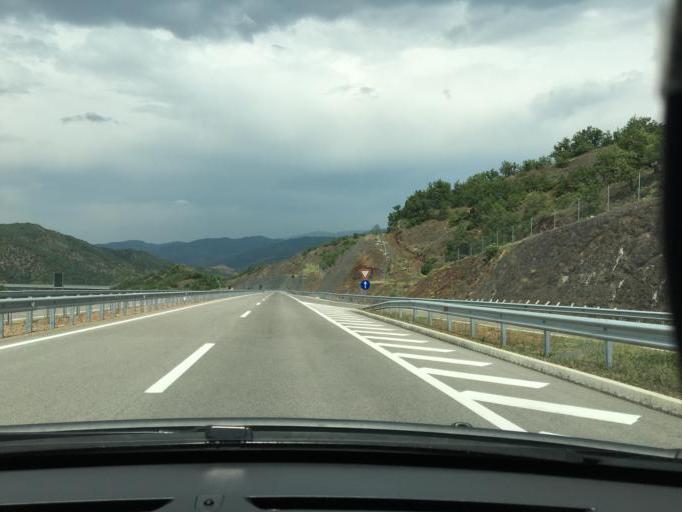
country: MK
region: Demir Kapija
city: Demir Kapija
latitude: 41.3639
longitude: 22.3447
